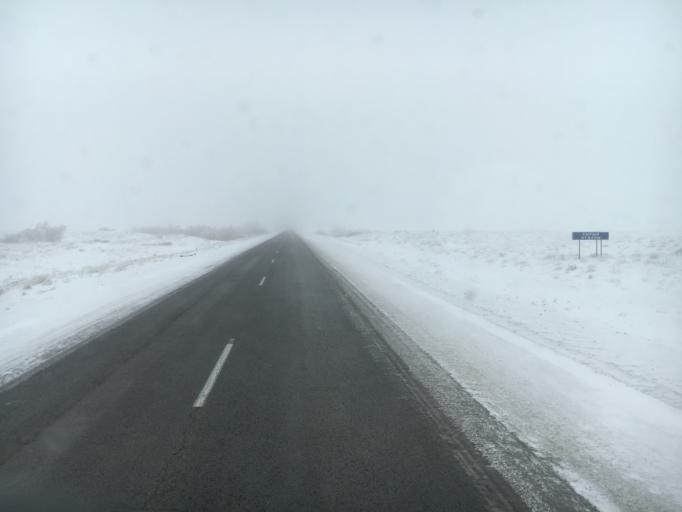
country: KZ
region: Batys Qazaqstan
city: Dzhambeyty
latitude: 50.1853
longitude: 53.3686
